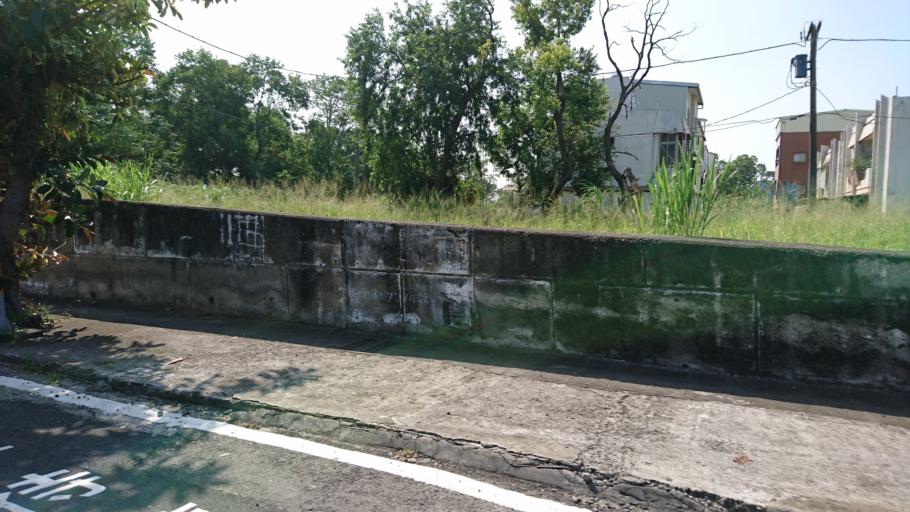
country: TW
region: Taiwan
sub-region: Hsinchu
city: Hsinchu
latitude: 24.7066
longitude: 120.9256
